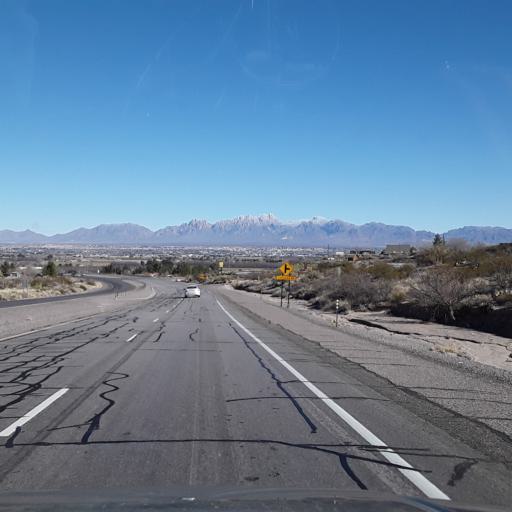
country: US
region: New Mexico
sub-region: Dona Ana County
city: Mesilla
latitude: 32.2926
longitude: -106.8642
